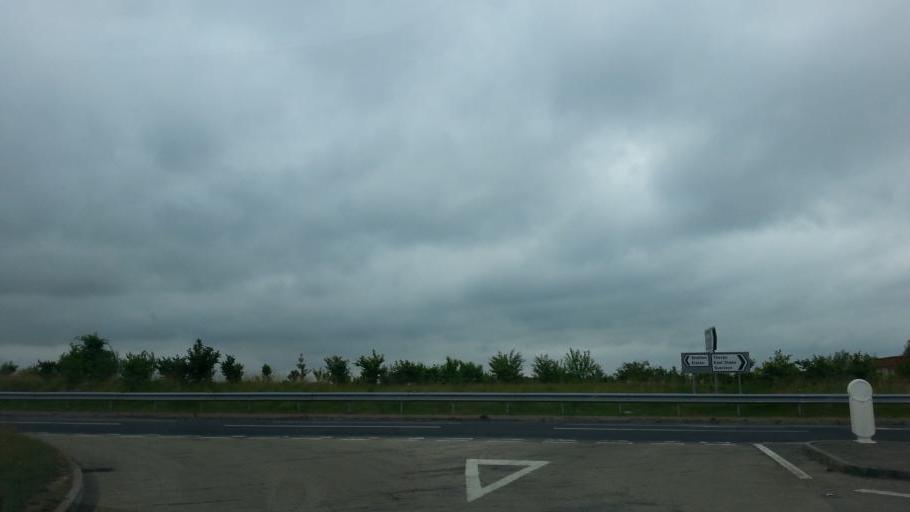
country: GB
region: England
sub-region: Nottinghamshire
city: Farndon
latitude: 53.0282
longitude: -0.8851
